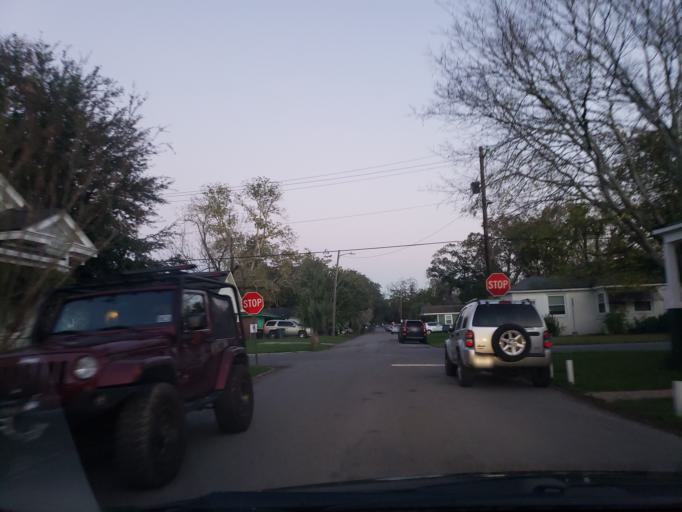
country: US
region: Georgia
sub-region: Chatham County
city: Savannah
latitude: 32.0527
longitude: -81.0883
